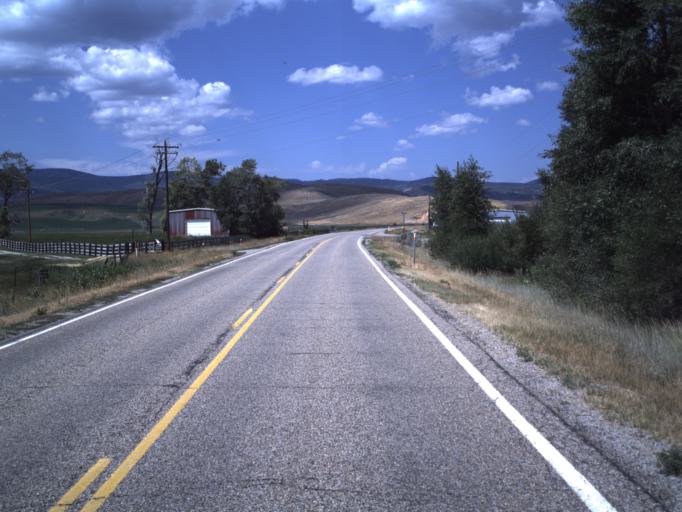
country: US
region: Utah
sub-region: Rich County
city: Randolph
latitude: 41.8389
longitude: -111.3398
